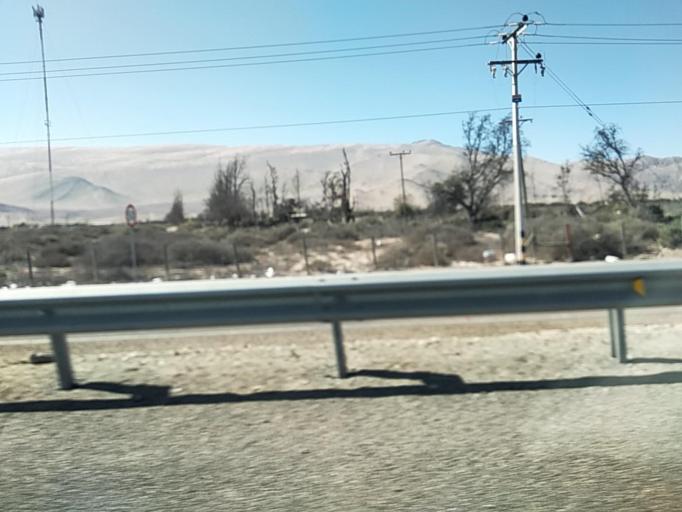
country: CL
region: Atacama
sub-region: Provincia de Copiapo
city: Copiapo
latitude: -27.2948
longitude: -70.4648
